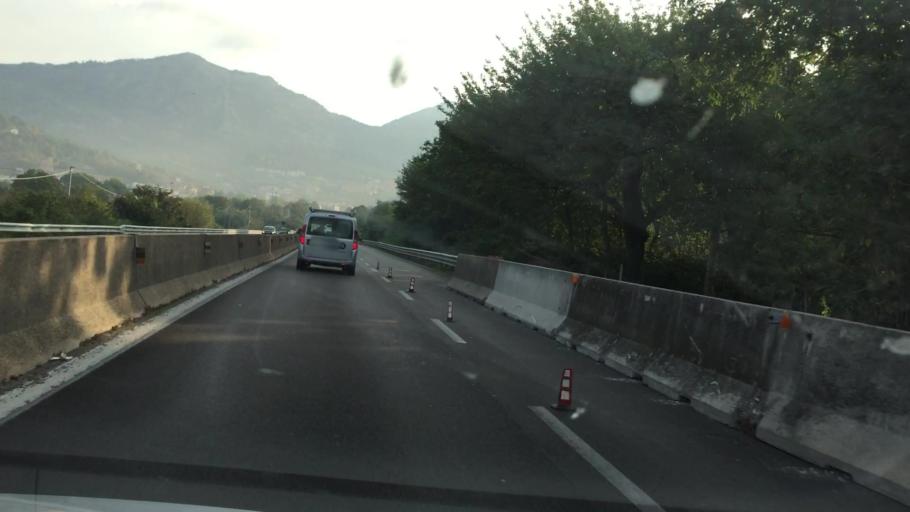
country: IT
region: Campania
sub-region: Provincia di Avellino
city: Torchiati
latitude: 40.8252
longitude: 14.8109
